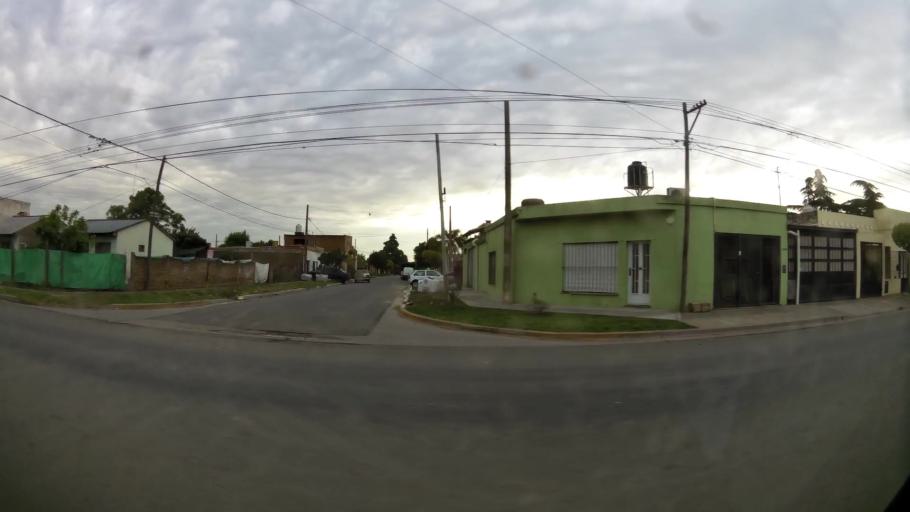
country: AR
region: Buenos Aires
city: San Nicolas de los Arroyos
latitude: -33.3614
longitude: -60.1945
